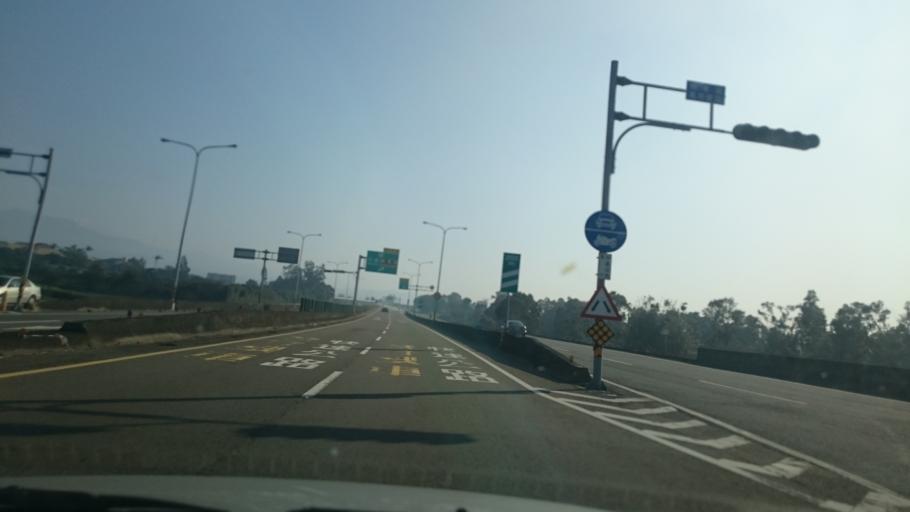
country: TW
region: Taiwan
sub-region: Hsinchu
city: Hsinchu
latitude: 24.7121
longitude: 120.8670
